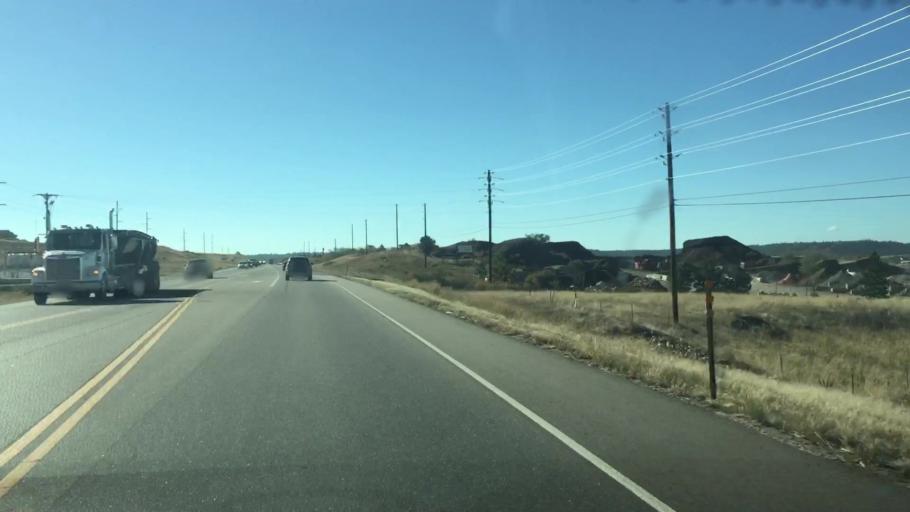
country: US
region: Colorado
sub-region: Douglas County
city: The Pinery
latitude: 39.4066
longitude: -104.7594
